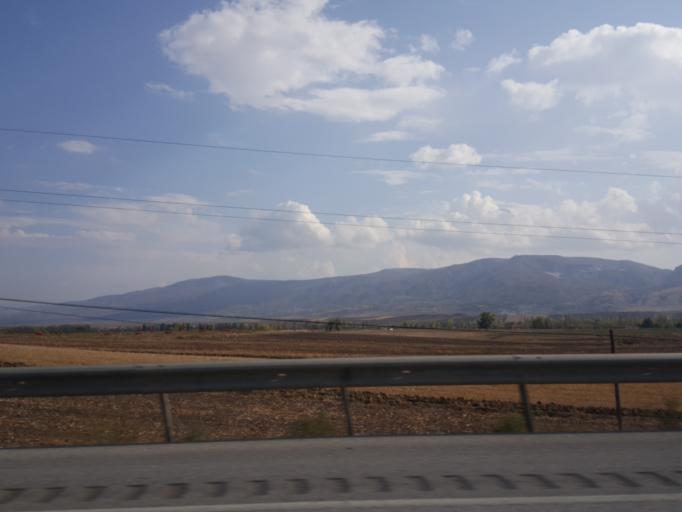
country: TR
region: Corum
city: Seydim
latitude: 40.4422
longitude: 34.8198
